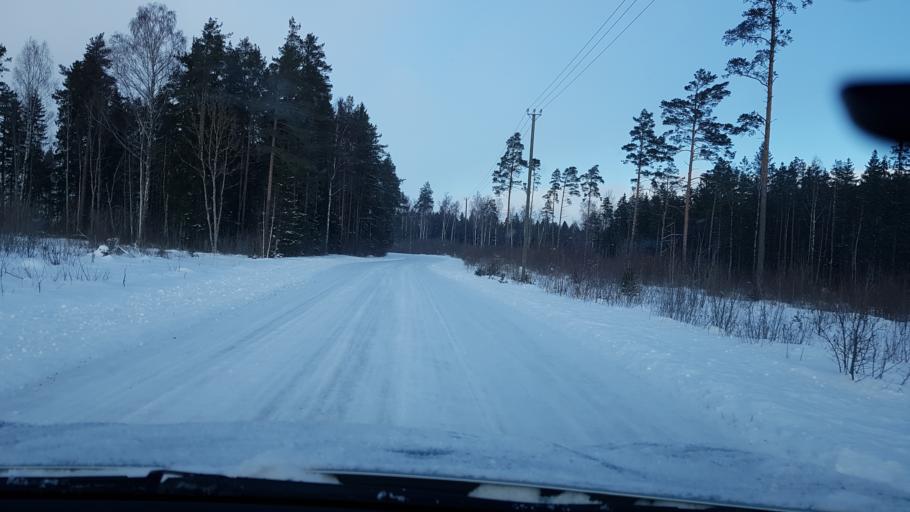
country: EE
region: Harju
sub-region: Nissi vald
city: Turba
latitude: 59.1924
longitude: 24.1398
